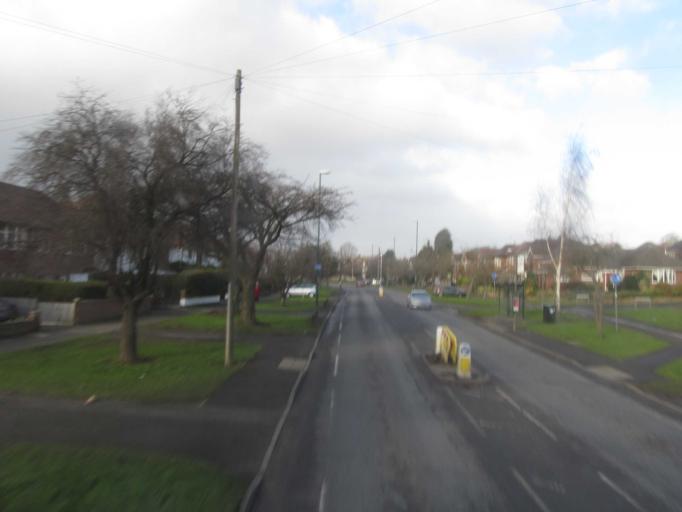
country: GB
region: England
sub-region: Nottinghamshire
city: Kimberley
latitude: 52.9437
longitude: -1.2242
